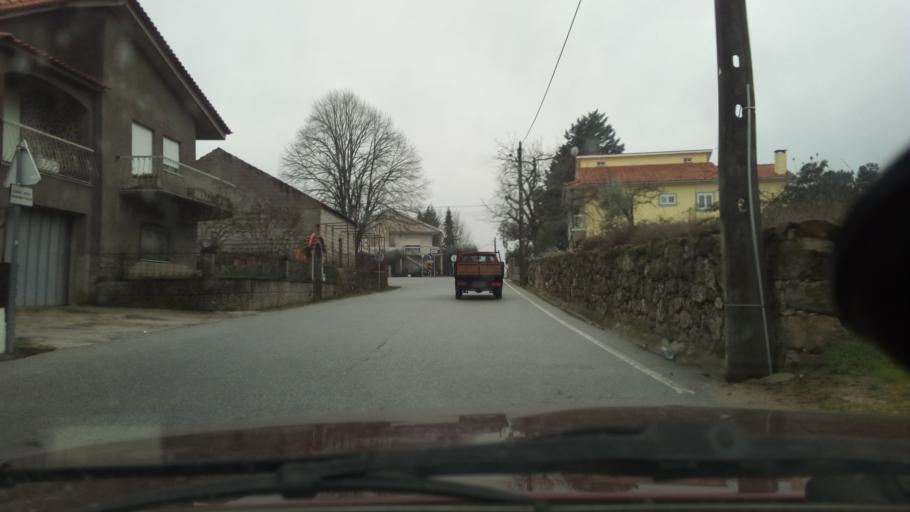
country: PT
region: Viseu
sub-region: Mangualde
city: Mangualde
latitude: 40.6049
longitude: -7.8206
